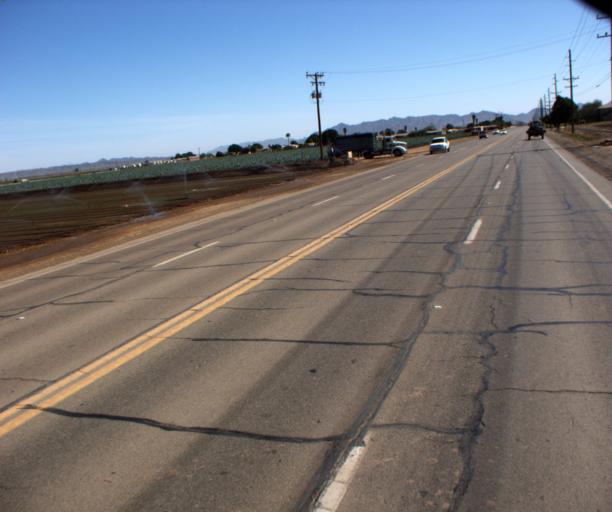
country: US
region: Arizona
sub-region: Yuma County
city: Yuma
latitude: 32.6991
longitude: -114.5352
